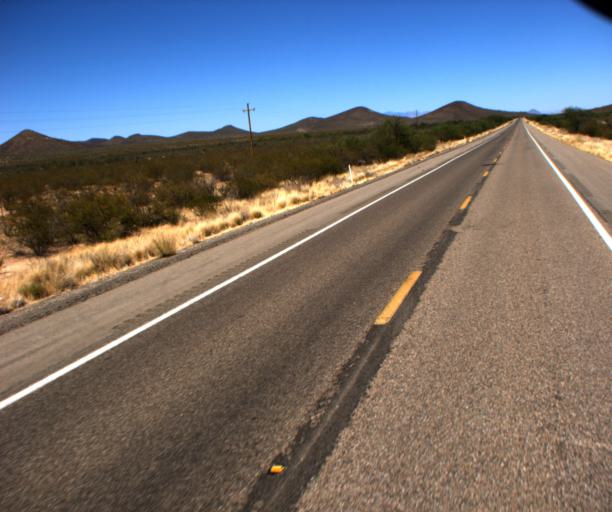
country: US
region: Arizona
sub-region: Pima County
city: Three Points
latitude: 32.0539
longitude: -111.4115
